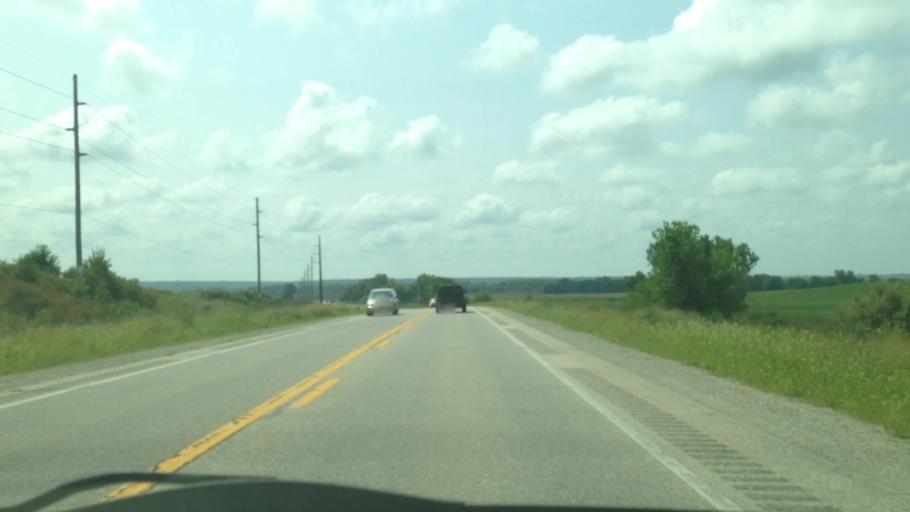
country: US
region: Iowa
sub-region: Benton County
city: Walford
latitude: 41.8230
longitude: -91.8731
